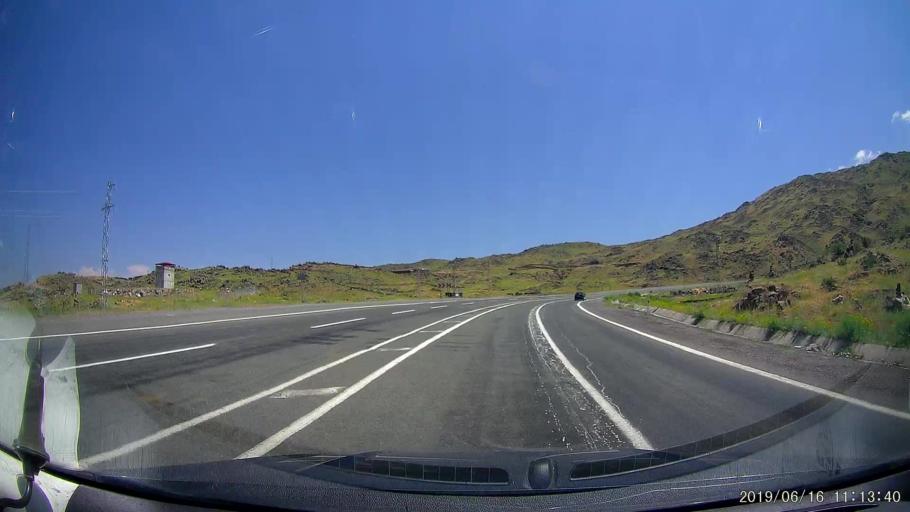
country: TR
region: Igdir
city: Igdir
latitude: 39.7859
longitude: 44.1416
